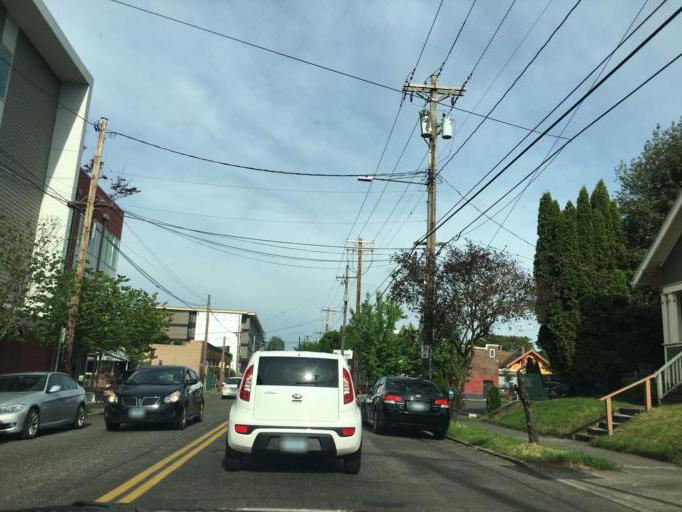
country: US
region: Oregon
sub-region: Multnomah County
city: Lents
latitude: 45.5053
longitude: -122.6138
